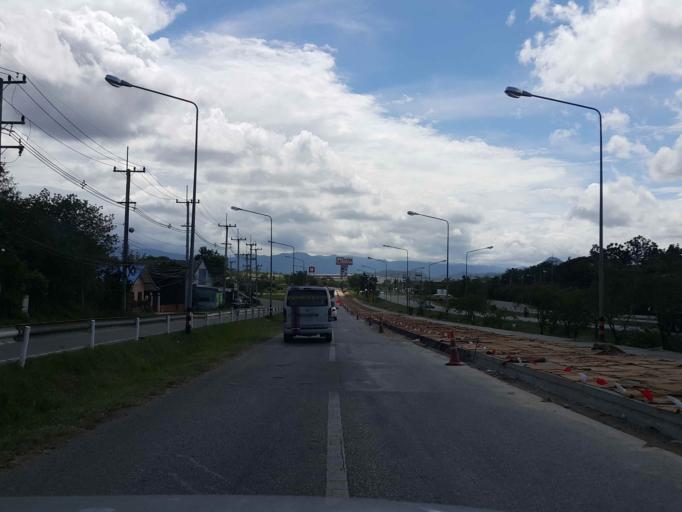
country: TH
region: Tak
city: Tak
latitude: 16.8549
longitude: 99.1215
